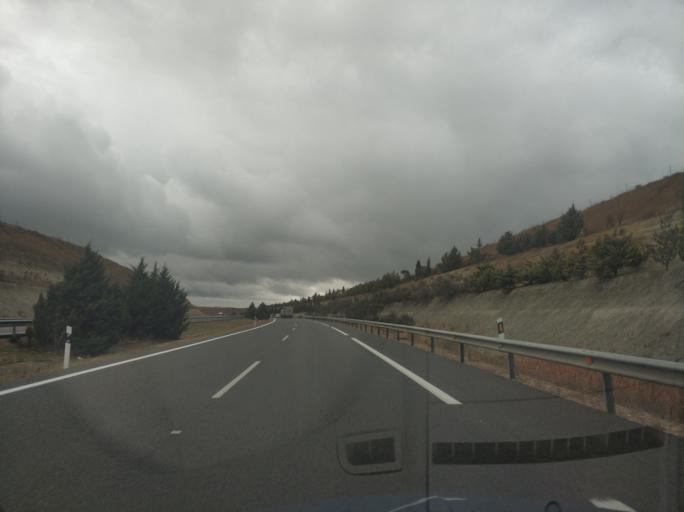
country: ES
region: Castille and Leon
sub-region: Provincia de Palencia
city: Soto de Cerrato
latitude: 41.9709
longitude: -4.4539
